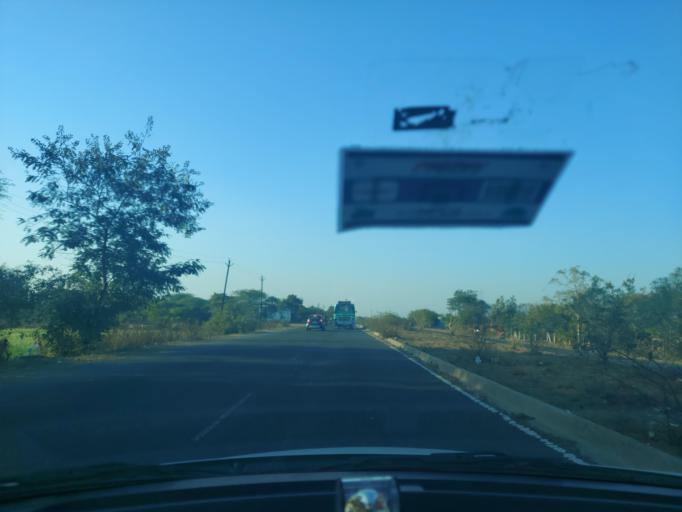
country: IN
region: Madhya Pradesh
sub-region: Indore
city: Sanwer
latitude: 23.0212
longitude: 75.8323
